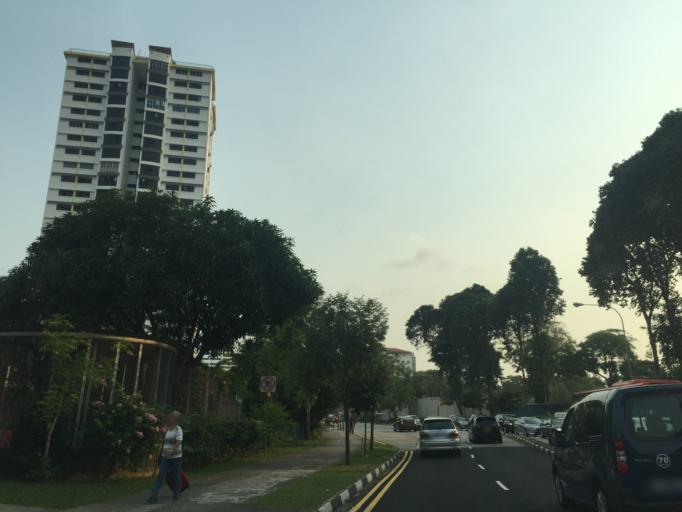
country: SG
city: Singapore
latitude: 1.3087
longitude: 103.7895
